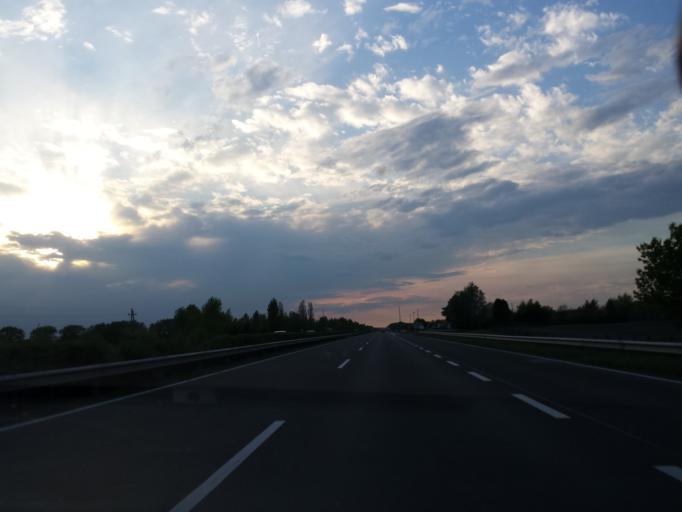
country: HU
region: Gyor-Moson-Sopron
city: Otteveny
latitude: 47.7045
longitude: 17.4923
